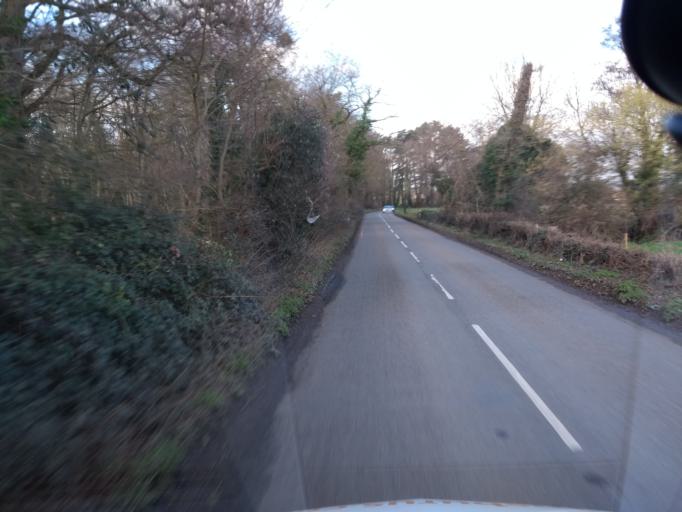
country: GB
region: England
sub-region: Somerset
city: Taunton
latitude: 50.9896
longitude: -3.0728
